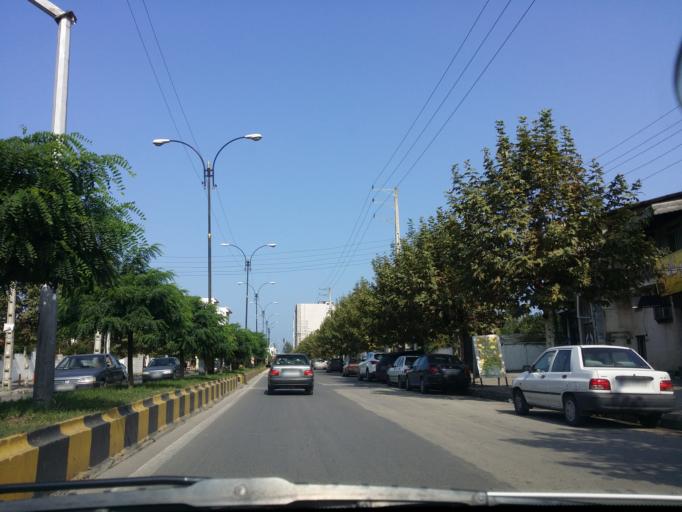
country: IR
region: Mazandaran
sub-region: Nowshahr
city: Nowshahr
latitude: 36.6419
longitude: 51.4909
